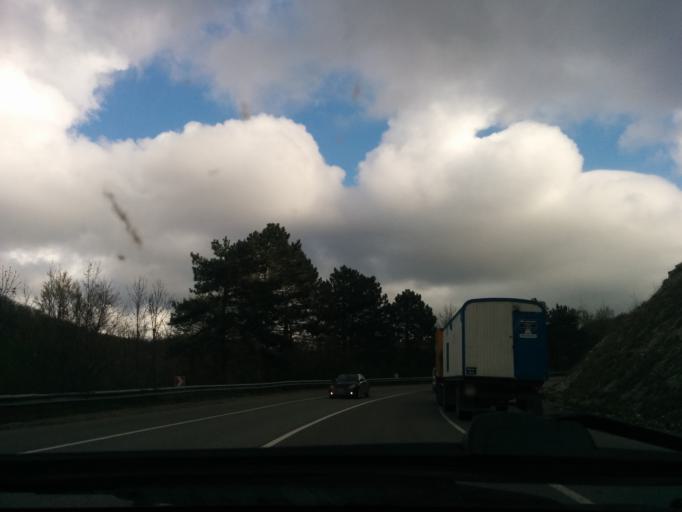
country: RU
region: Krasnodarskiy
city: Novomikhaylovskiy
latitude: 44.2567
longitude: 38.8827
